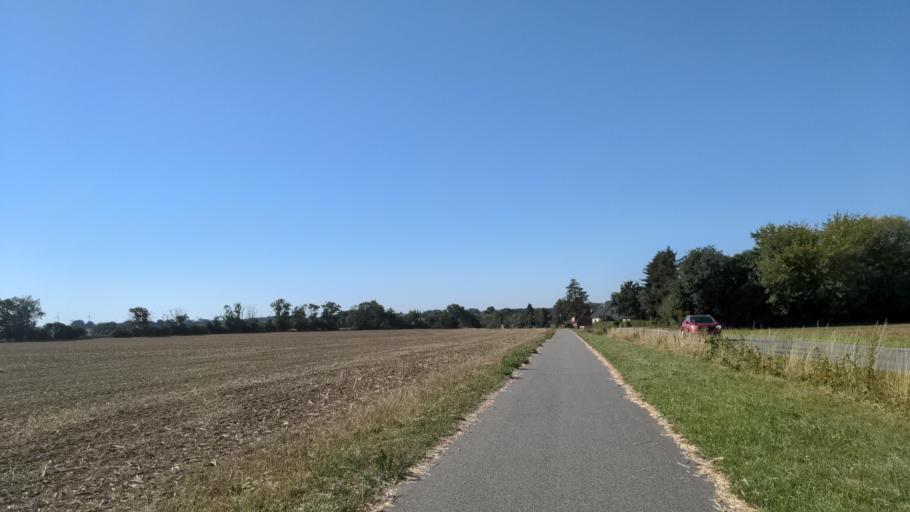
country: DE
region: Mecklenburg-Vorpommern
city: Gramkow
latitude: 53.9393
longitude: 11.3310
